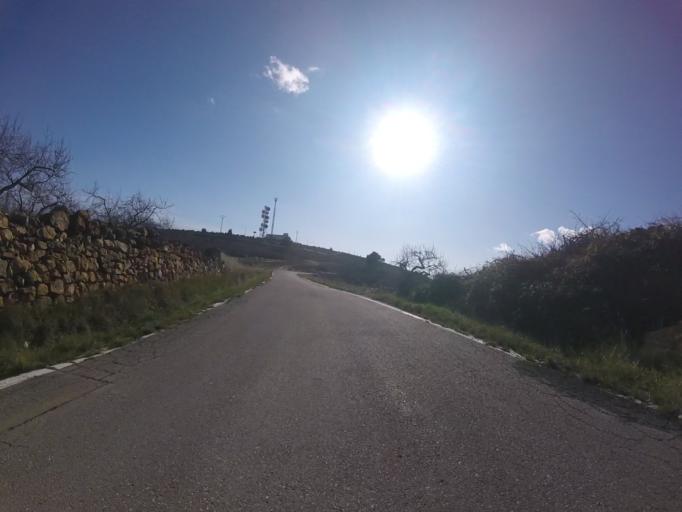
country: ES
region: Valencia
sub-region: Provincia de Castello
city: Sarratella
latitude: 40.3028
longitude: 0.0304
